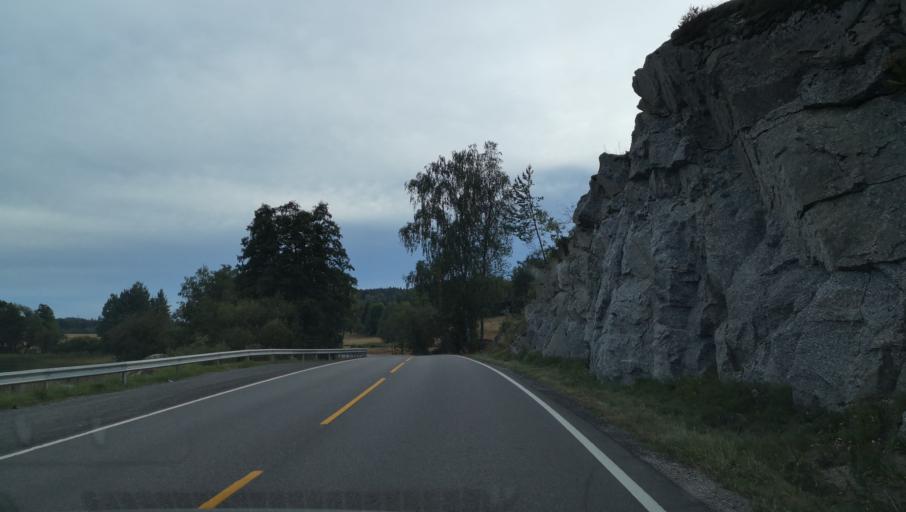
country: NO
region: Ostfold
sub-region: Hobol
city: Tomter
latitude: 59.6990
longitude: 11.0431
